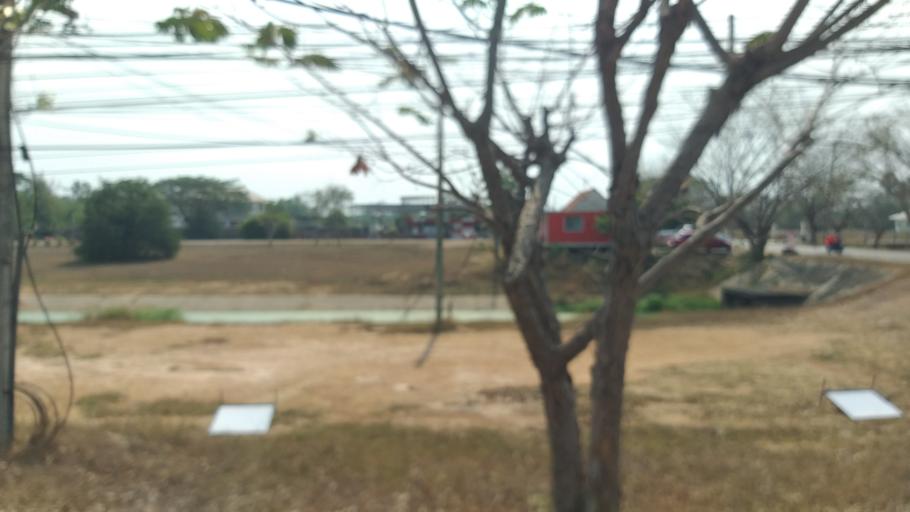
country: TH
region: Changwat Udon Thani
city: Udon Thani
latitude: 17.3857
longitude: 102.7754
